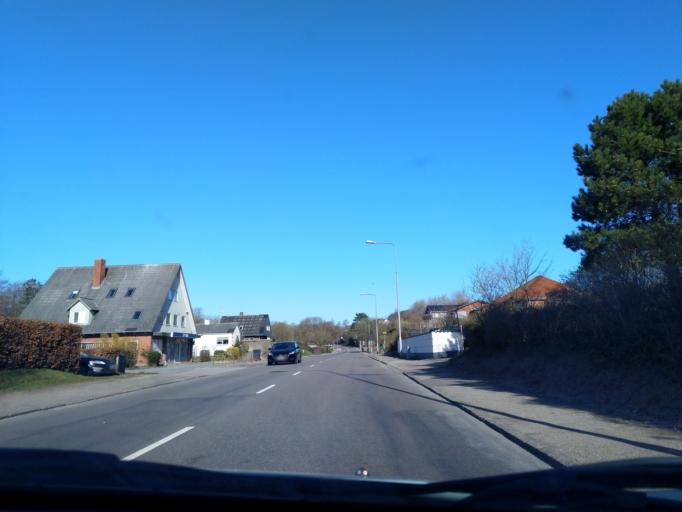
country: DK
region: Zealand
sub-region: Kalundborg Kommune
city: Kalundborg
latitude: 55.6973
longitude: 11.0413
